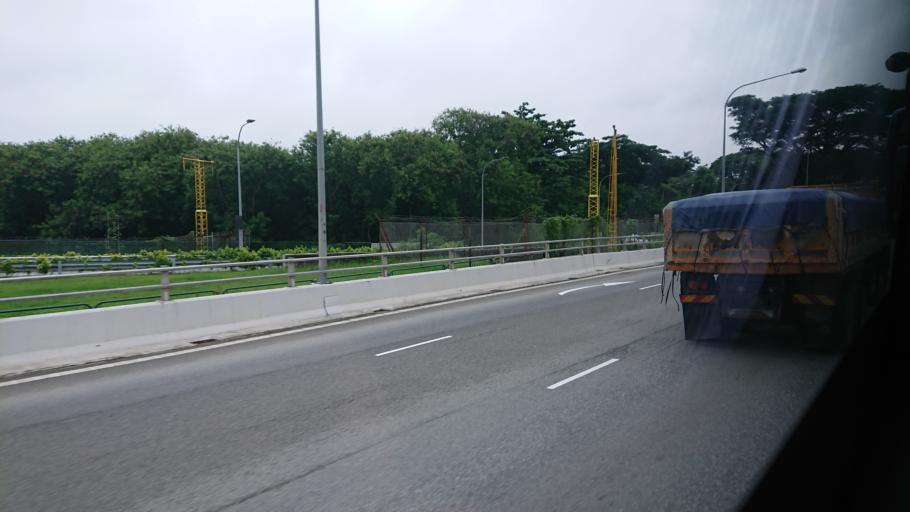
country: MY
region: Johor
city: Kampung Pasir Gudang Baru
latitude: 1.3818
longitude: 103.9183
